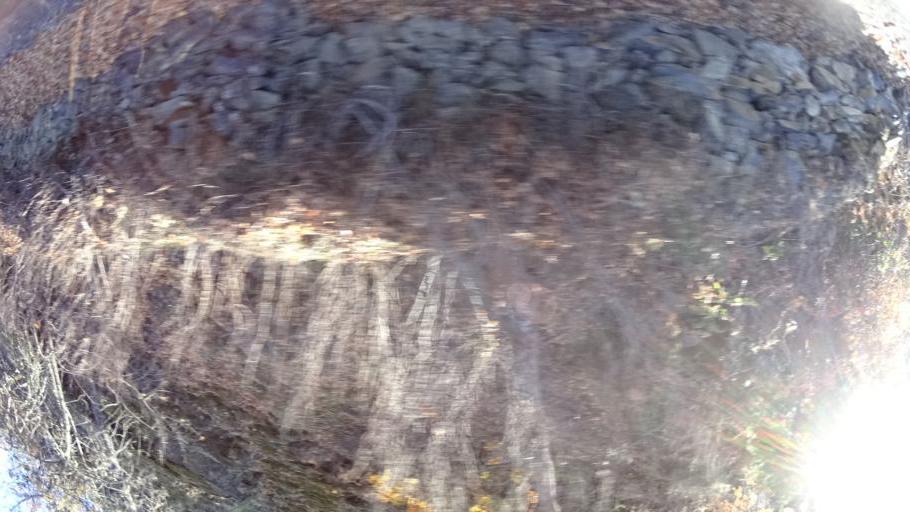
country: US
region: California
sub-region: Siskiyou County
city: Yreka
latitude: 41.8329
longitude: -122.8518
